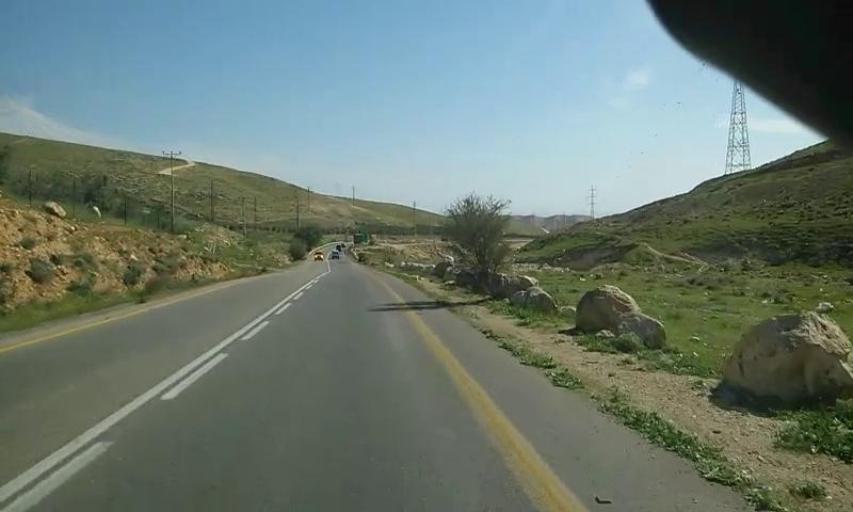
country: PS
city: Az Za`ayyim
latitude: 31.8084
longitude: 35.3174
